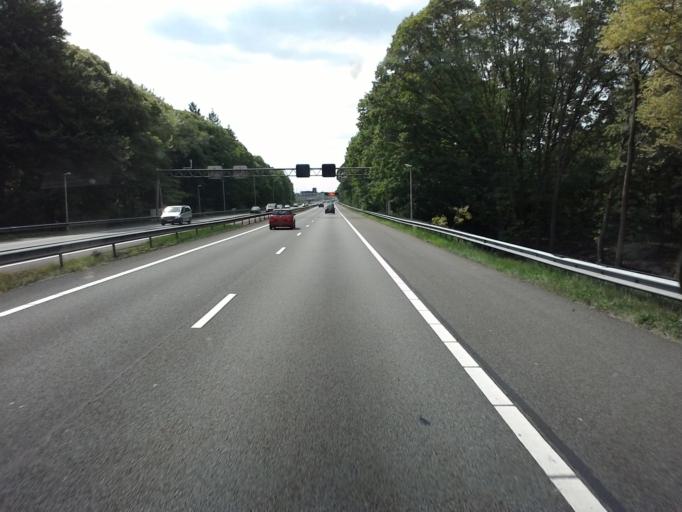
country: NL
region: Gelderland
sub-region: Gemeente Ede
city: Bennekom
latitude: 52.0127
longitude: 5.6876
